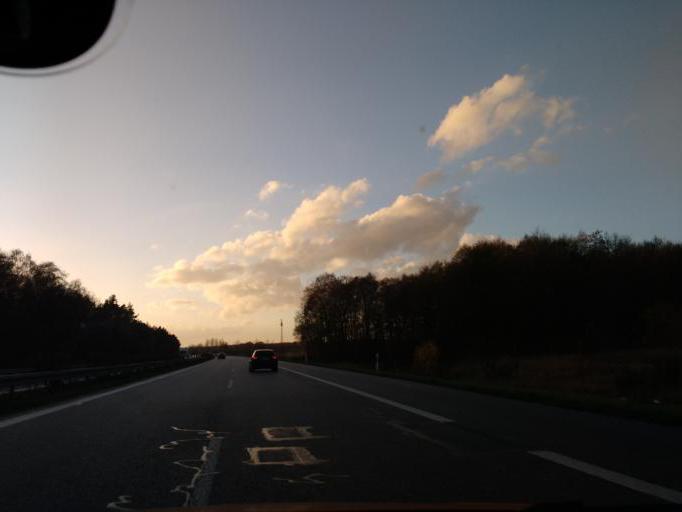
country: DE
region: Mecklenburg-Vorpommern
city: Hagenow
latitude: 53.4883
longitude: 11.2487
